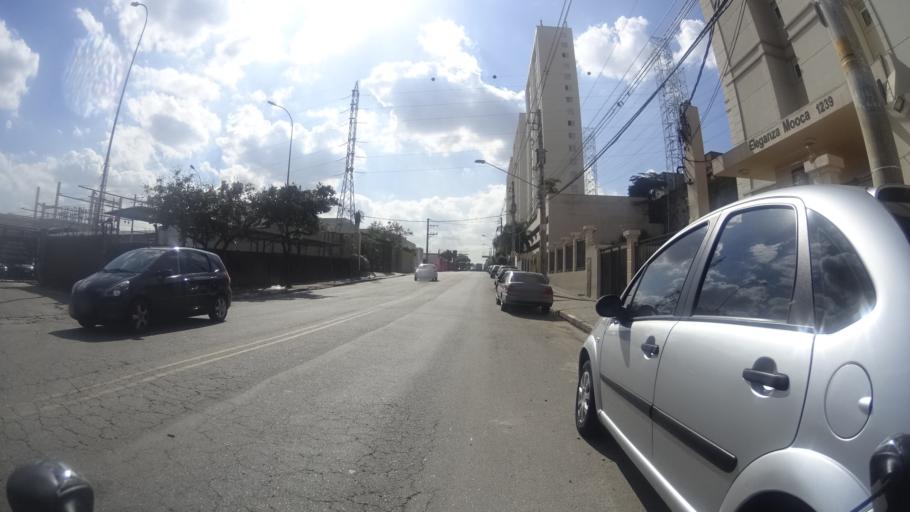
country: BR
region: Sao Paulo
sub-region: Sao Paulo
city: Sao Paulo
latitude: -23.5795
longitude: -46.5920
